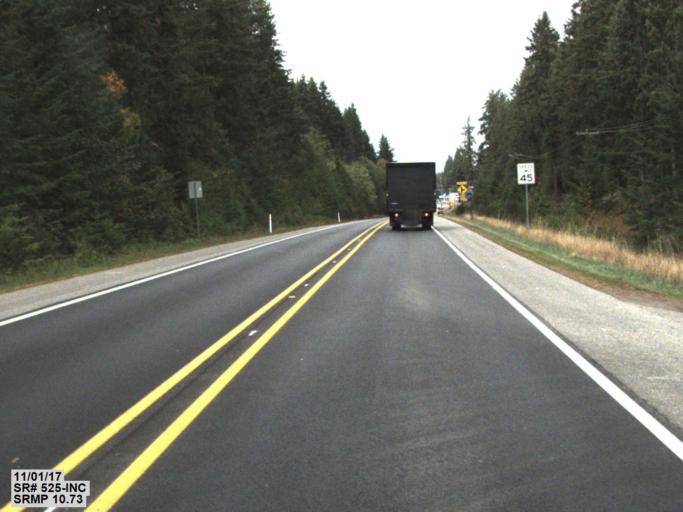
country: US
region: Washington
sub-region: Island County
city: Langley
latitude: 47.9867
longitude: -122.3923
